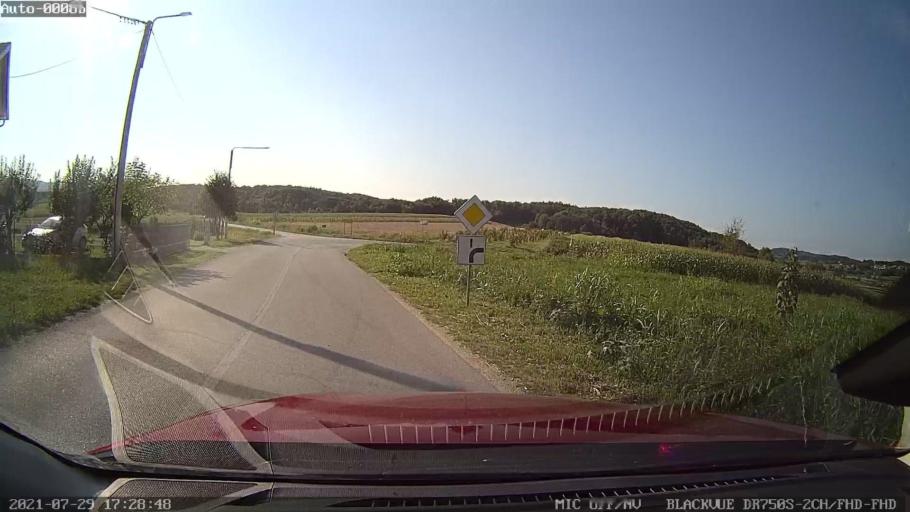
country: HR
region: Varazdinska
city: Klenovnik
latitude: 46.2694
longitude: 16.1149
